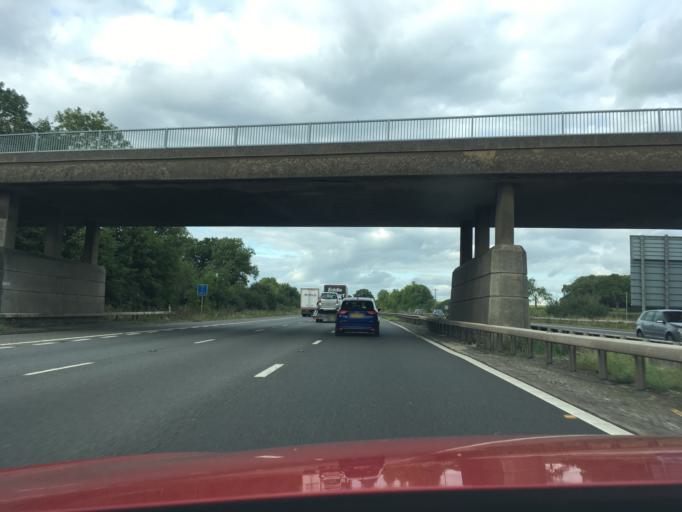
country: GB
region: England
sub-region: Gloucestershire
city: Stonehouse
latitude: 51.7636
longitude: -2.3180
